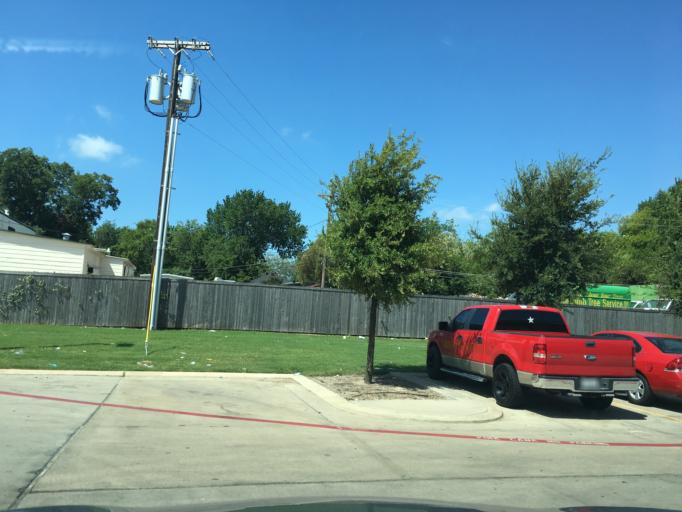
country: US
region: Texas
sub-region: Dallas County
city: Garland
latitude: 32.8422
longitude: -96.6659
